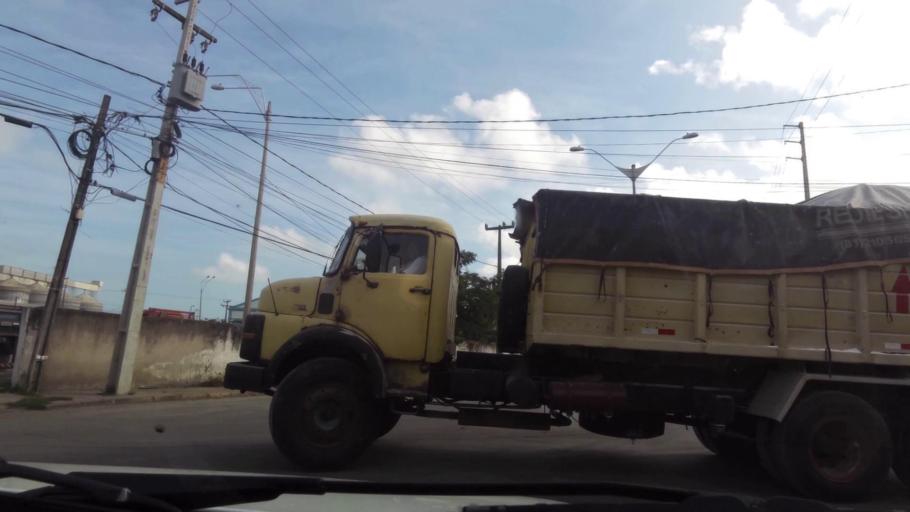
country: BR
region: Pernambuco
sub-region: Recife
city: Recife
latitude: -8.0514
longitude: -34.8711
